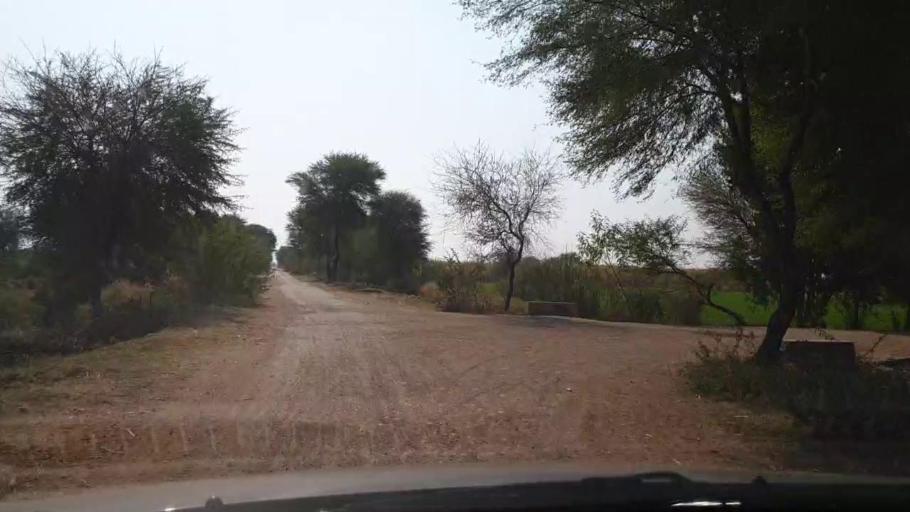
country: PK
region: Sindh
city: Jhol
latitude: 25.8386
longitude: 68.9874
